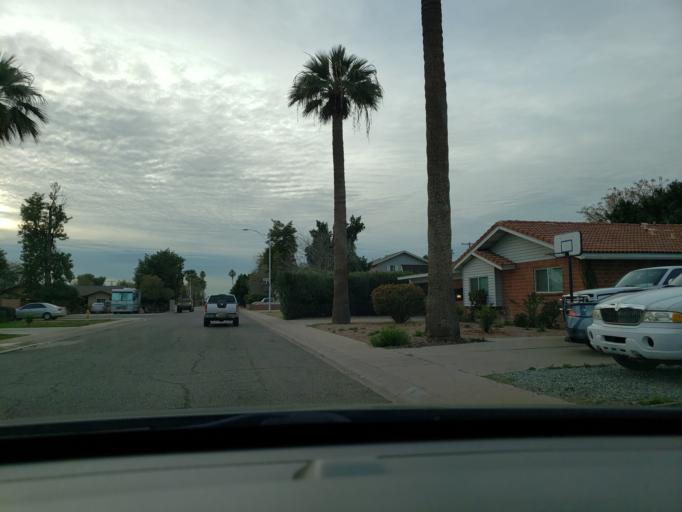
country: US
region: Arizona
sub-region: Maricopa County
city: Glendale
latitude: 33.5327
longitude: -112.1349
